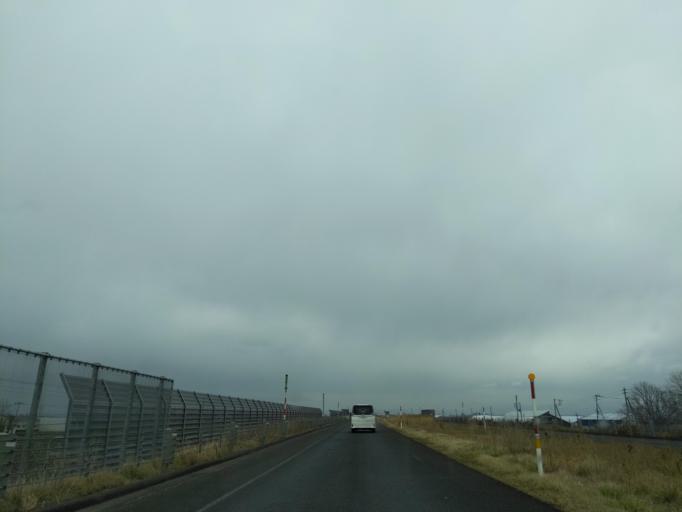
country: JP
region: Hokkaido
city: Tobetsu
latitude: 43.1857
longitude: 141.5377
